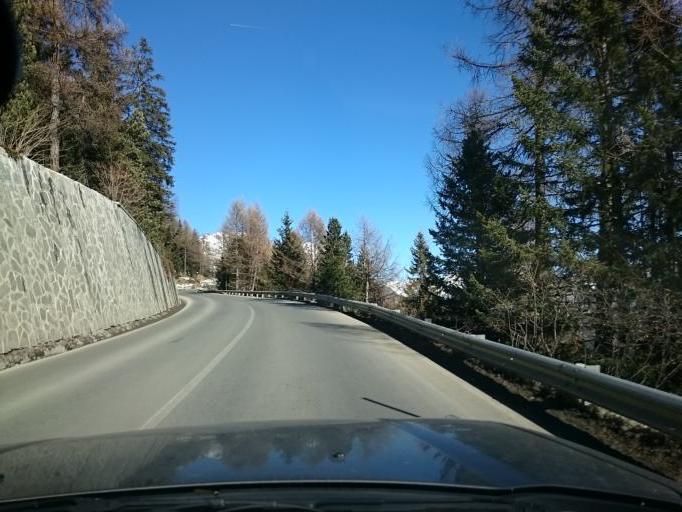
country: IT
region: Lombardy
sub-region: Provincia di Sondrio
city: Isolaccia
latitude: 46.4707
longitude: 10.2506
